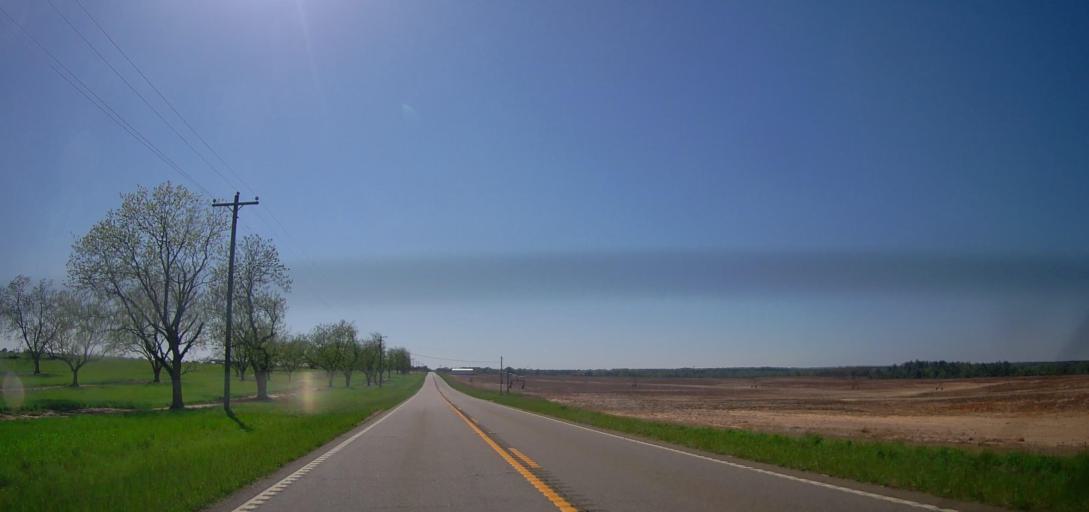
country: US
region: Georgia
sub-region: Dooly County
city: Unadilla
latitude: 32.2599
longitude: -83.6634
